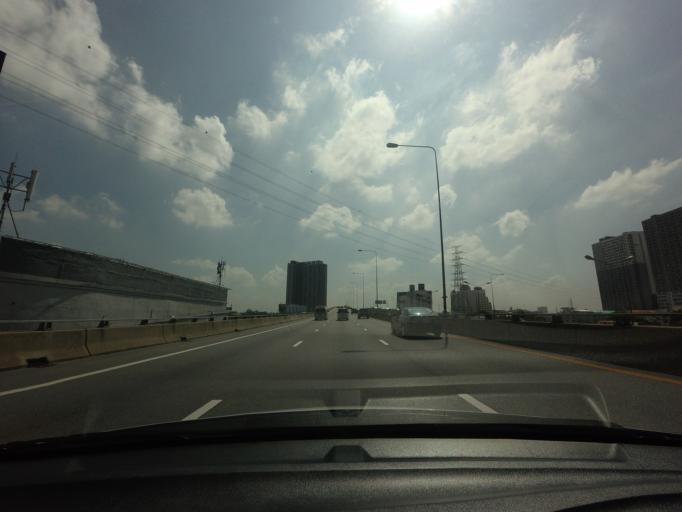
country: TH
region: Bangkok
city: Watthana
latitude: 13.7494
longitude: 100.6004
